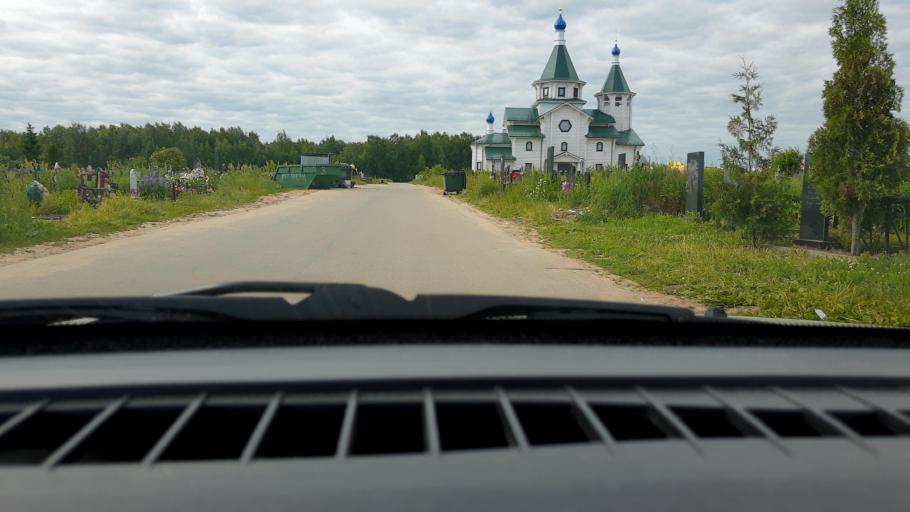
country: RU
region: Nizjnij Novgorod
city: Afonino
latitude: 56.2306
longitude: 44.0775
